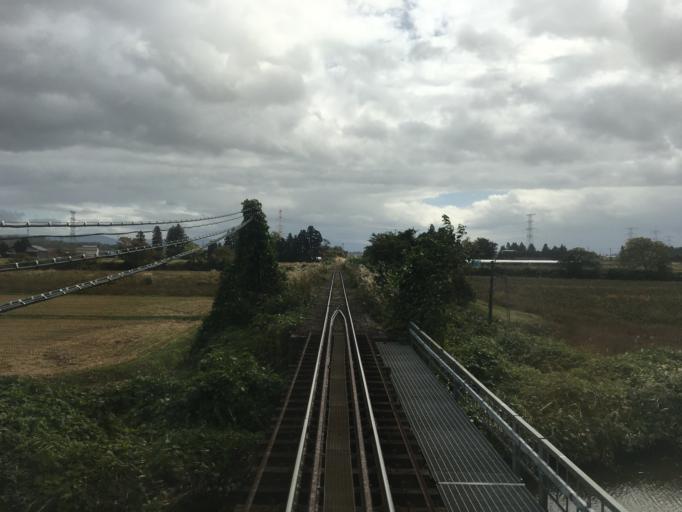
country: JP
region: Yamagata
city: Nagai
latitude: 38.0658
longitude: 140.0346
